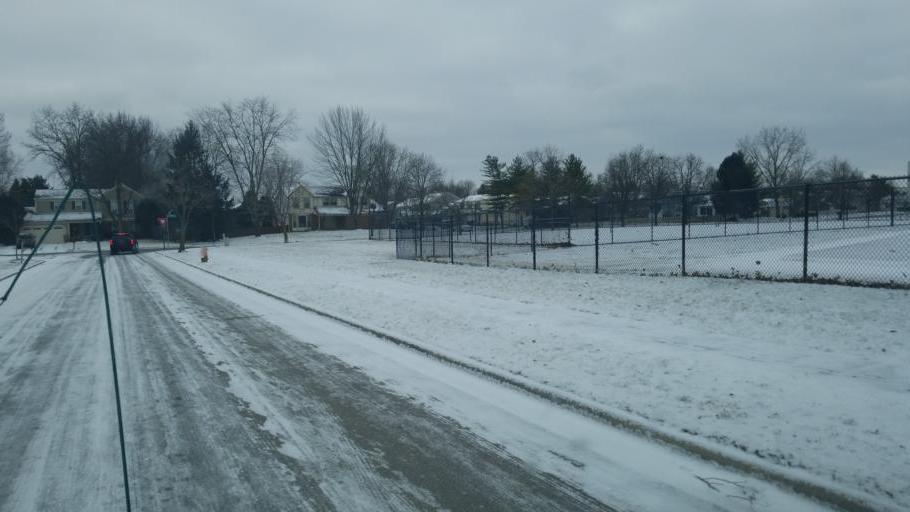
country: US
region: Ohio
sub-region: Delaware County
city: Powell
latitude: 40.1207
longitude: -83.0764
